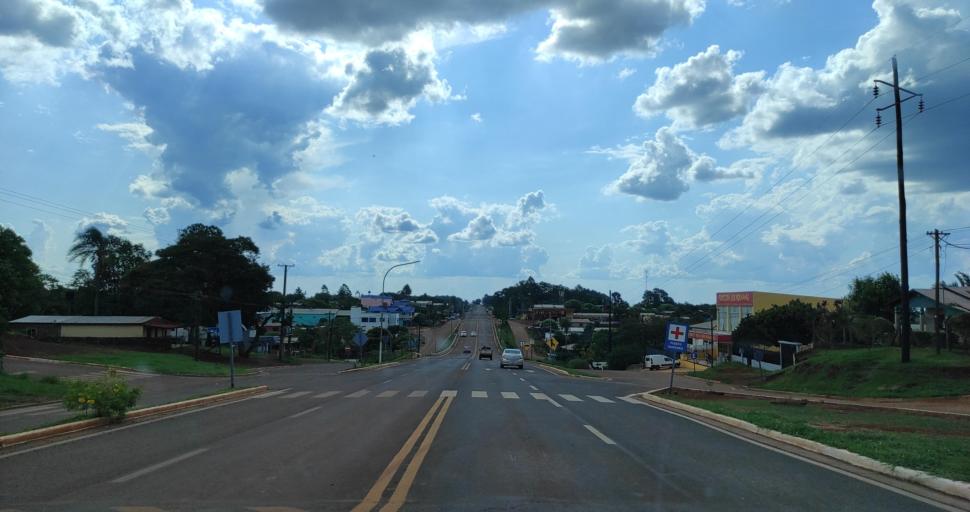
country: AR
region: Misiones
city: Bernardo de Irigoyen
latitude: -26.2953
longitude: -53.7522
